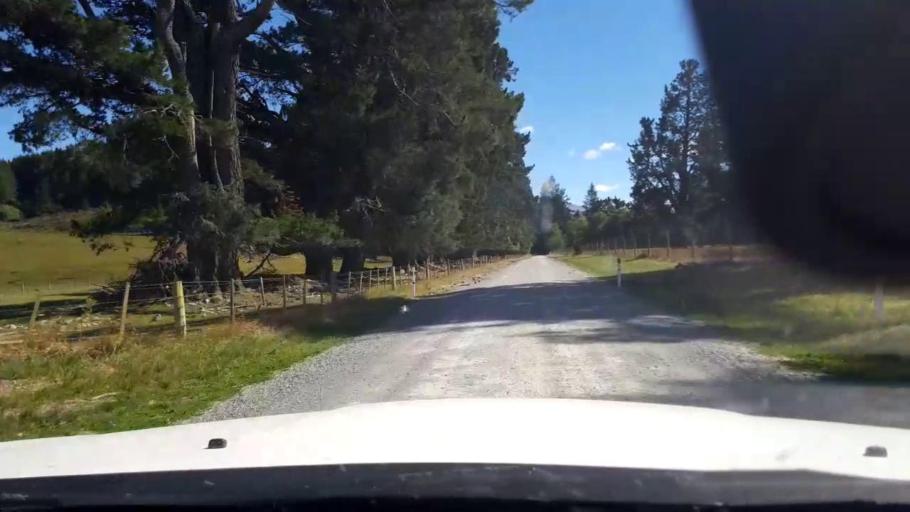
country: NZ
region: Canterbury
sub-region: Timaru District
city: Pleasant Point
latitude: -44.0287
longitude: 170.7435
